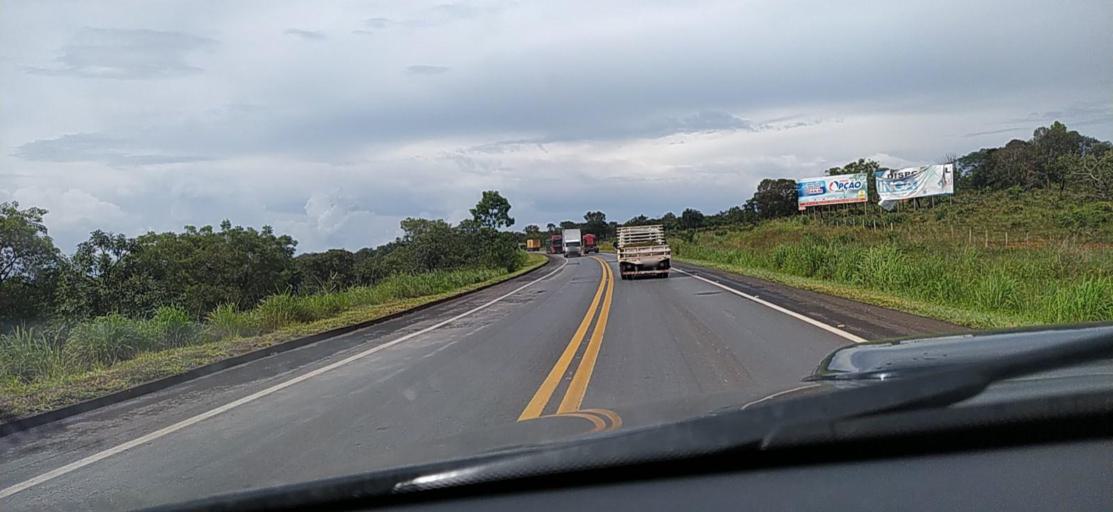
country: BR
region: Minas Gerais
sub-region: Montes Claros
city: Montes Claros
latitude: -16.8696
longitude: -43.8548
